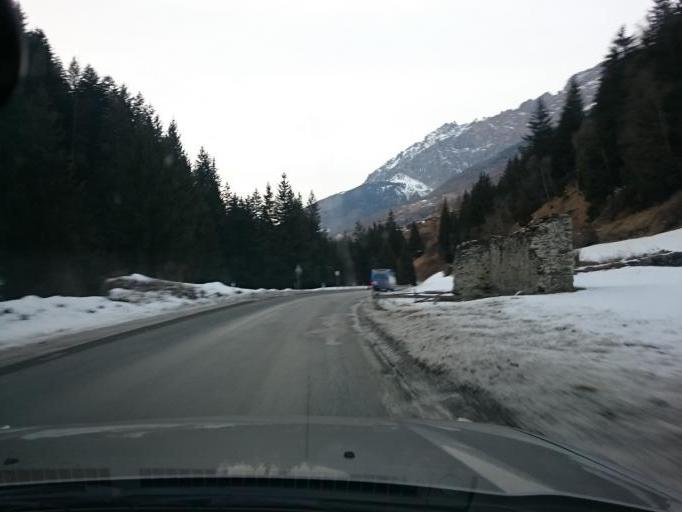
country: IT
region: Lombardy
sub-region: Provincia di Sondrio
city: Sant'Antonio
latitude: 46.4504
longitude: 10.4373
